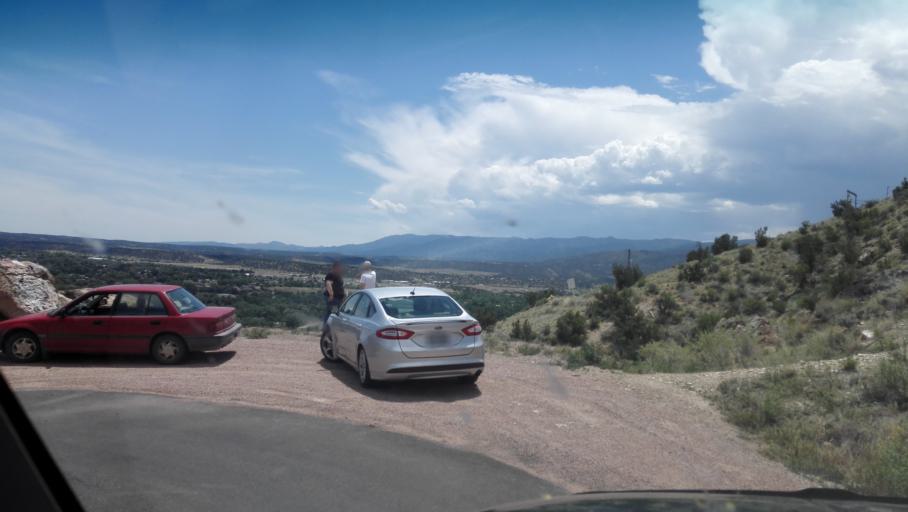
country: US
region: Colorado
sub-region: Fremont County
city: Canon City
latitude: 38.4453
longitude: -105.2495
